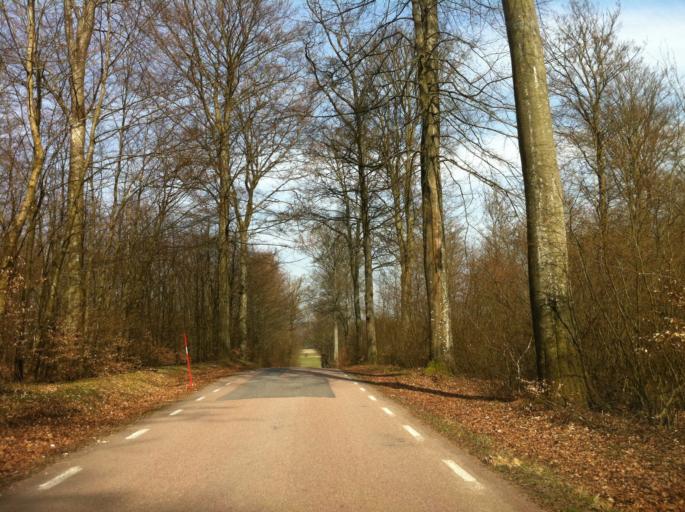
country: SE
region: Skane
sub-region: Klippans Kommun
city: Ljungbyhed
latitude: 55.9887
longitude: 13.2026
